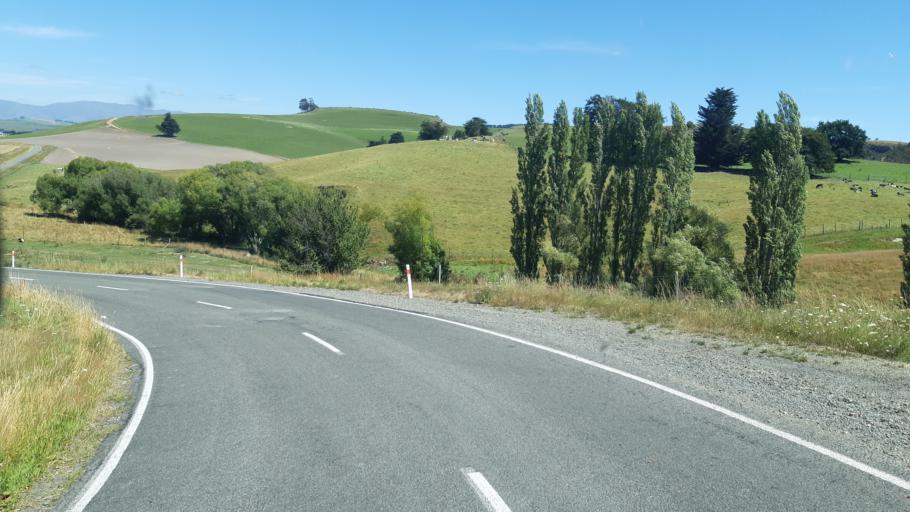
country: NZ
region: Canterbury
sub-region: Timaru District
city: Timaru
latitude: -44.4166
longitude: 171.1278
